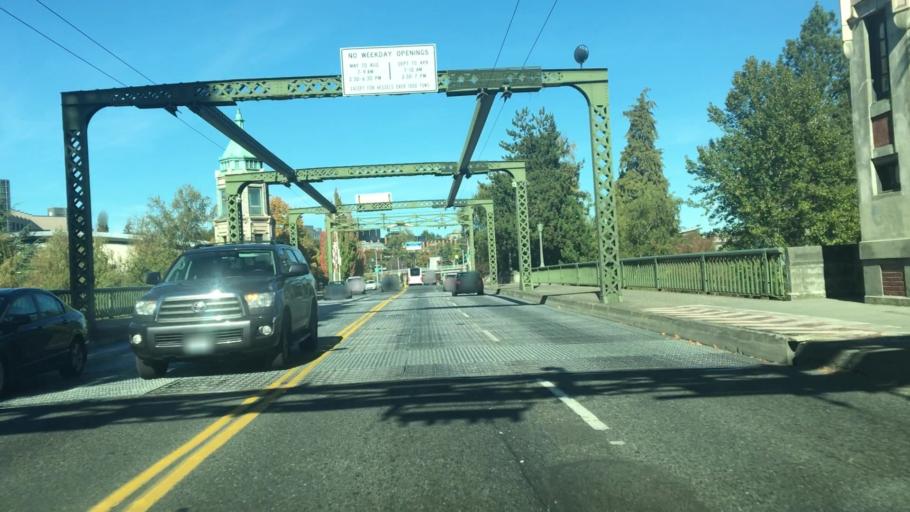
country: US
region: Washington
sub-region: King County
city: Seattle
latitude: 47.6470
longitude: -122.3046
